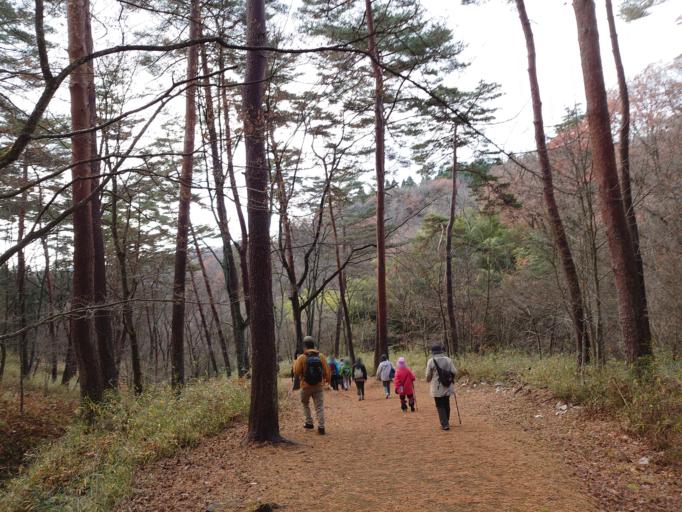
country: JP
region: Iwate
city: Ichinoseki
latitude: 38.9915
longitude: 141.1030
